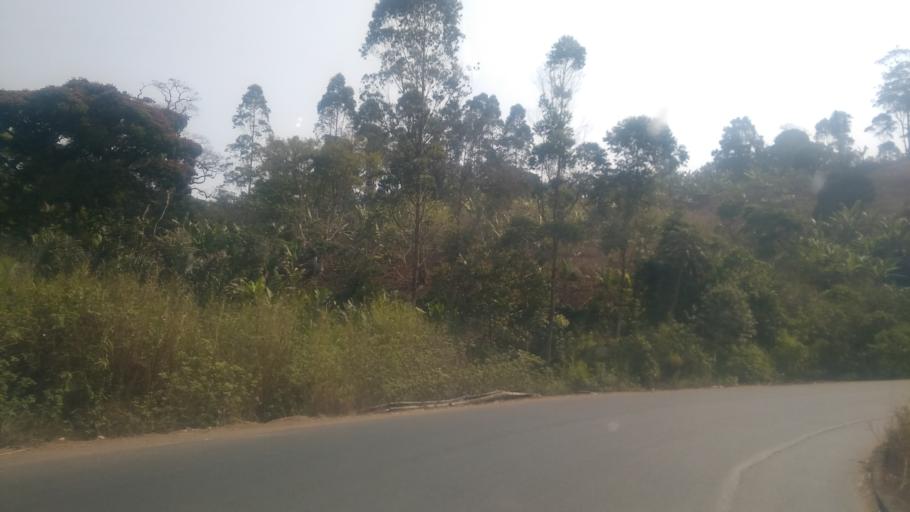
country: CM
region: West
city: Dschang
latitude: 5.4091
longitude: 10.0140
